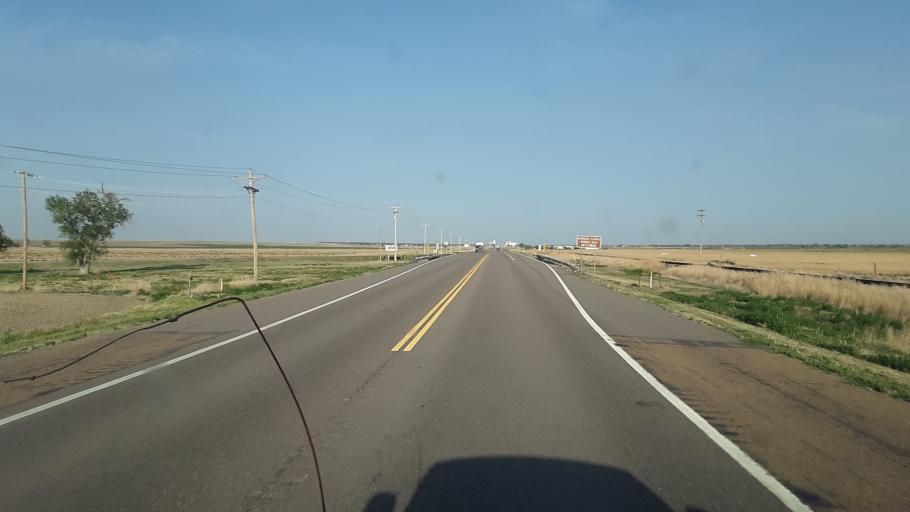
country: US
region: Kansas
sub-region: Hamilton County
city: Syracuse
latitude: 37.9971
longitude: -101.8181
